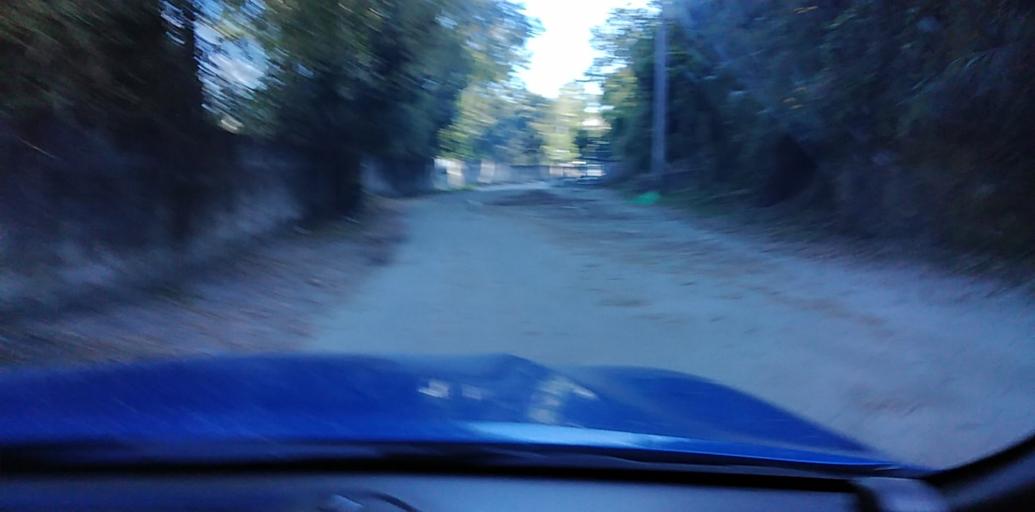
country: PH
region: Central Luzon
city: Santol
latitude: 15.1658
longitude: 120.4902
